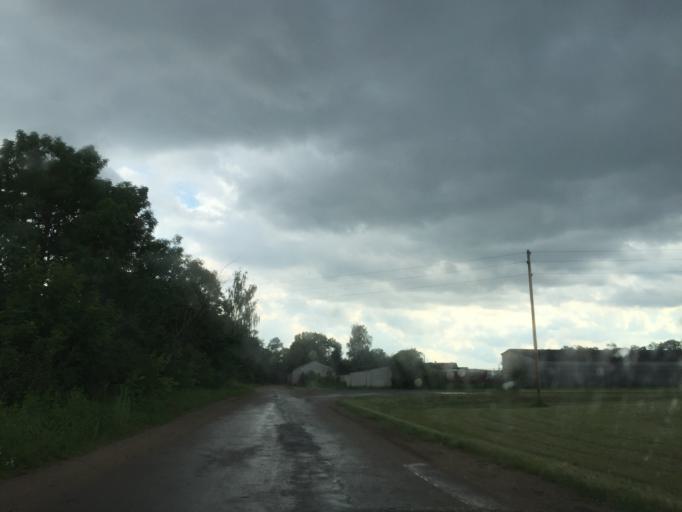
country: LV
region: Dobeles Rajons
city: Dobele
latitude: 56.6200
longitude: 23.3456
